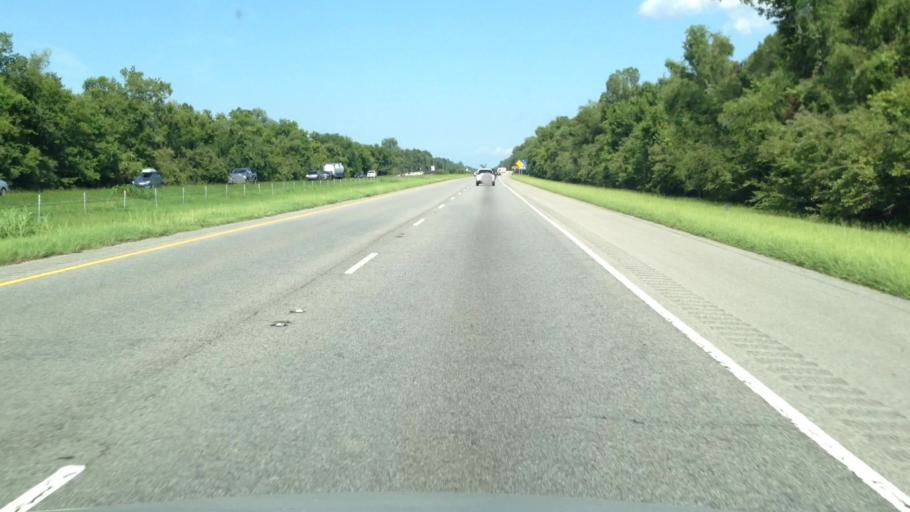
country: US
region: Louisiana
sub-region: Saint John the Baptist Parish
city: Reserve
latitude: 30.1131
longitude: -90.5686
